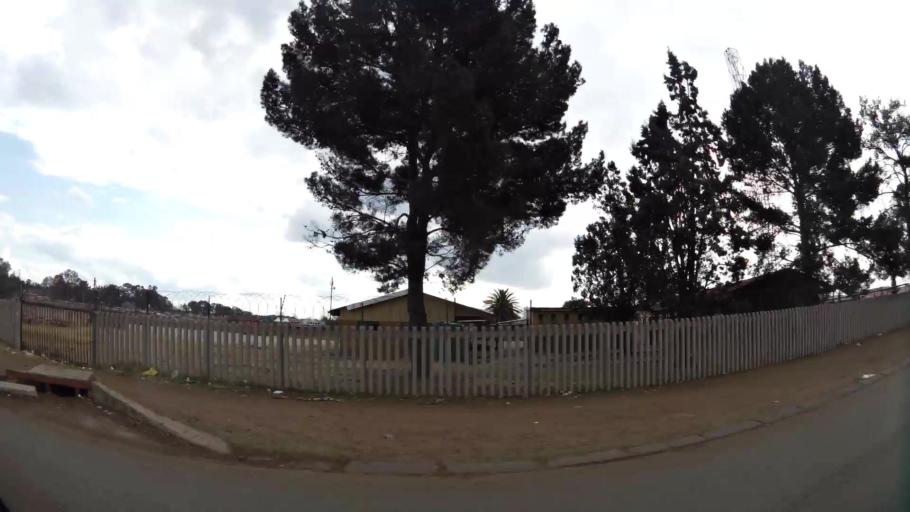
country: ZA
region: Gauteng
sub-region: Sedibeng District Municipality
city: Vanderbijlpark
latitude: -26.6688
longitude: 27.8494
